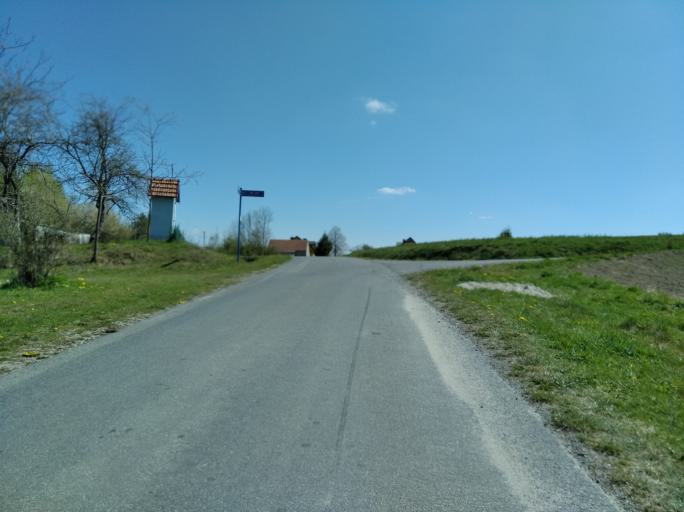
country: PL
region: Subcarpathian Voivodeship
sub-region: Powiat strzyzowski
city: Wisniowa
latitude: 49.9086
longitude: 21.6867
